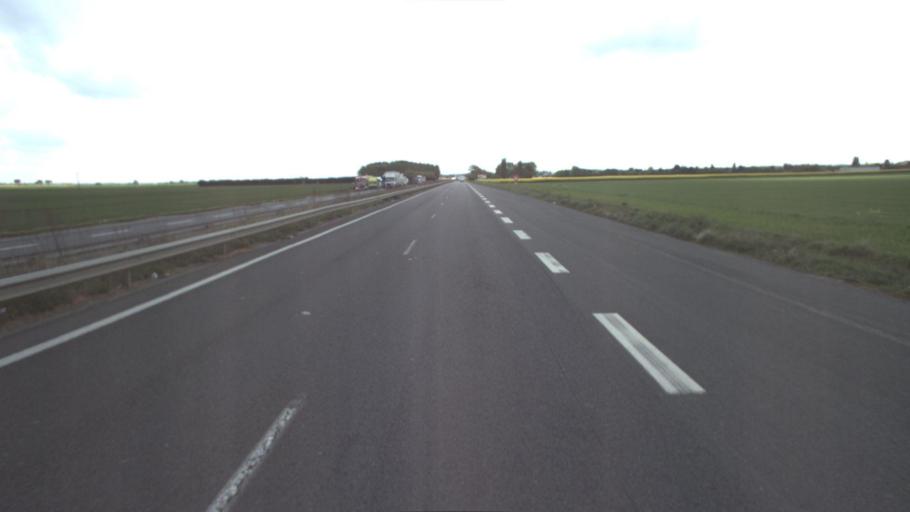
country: FR
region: Ile-de-France
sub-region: Departement de Seine-et-Marne
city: Rozay-en-Brie
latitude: 48.6920
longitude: 2.9153
